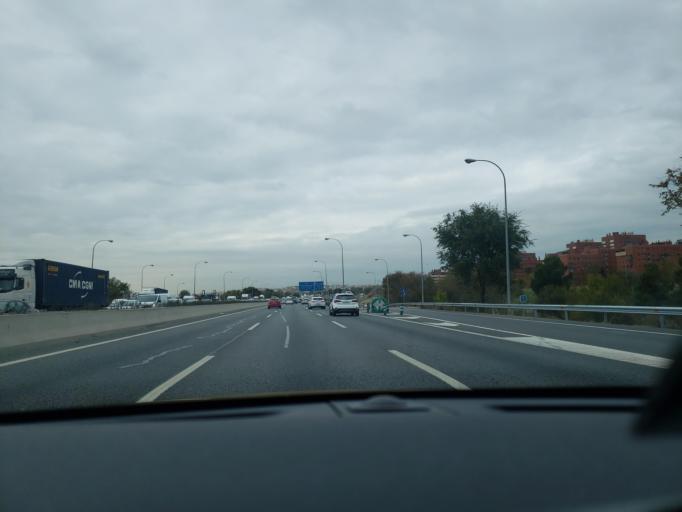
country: ES
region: Madrid
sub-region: Provincia de Madrid
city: Villaverde
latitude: 40.3639
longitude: -3.7107
